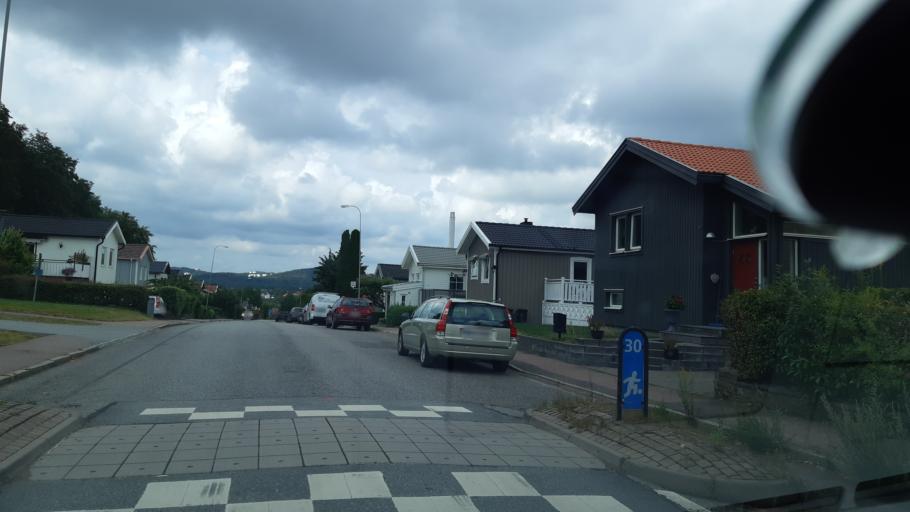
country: SE
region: Vaestra Goetaland
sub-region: Goteborg
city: Eriksbo
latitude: 57.7247
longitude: 12.0525
